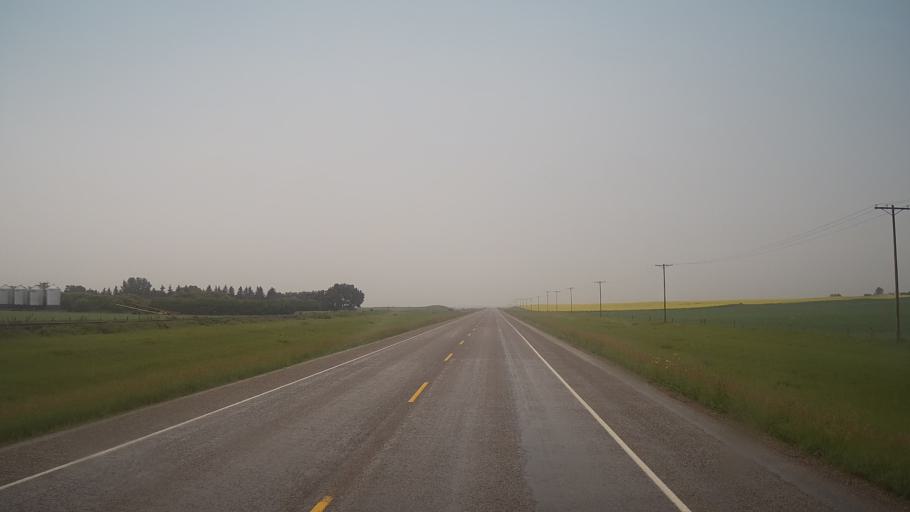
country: CA
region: Saskatchewan
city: Biggar
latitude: 52.1377
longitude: -108.1755
